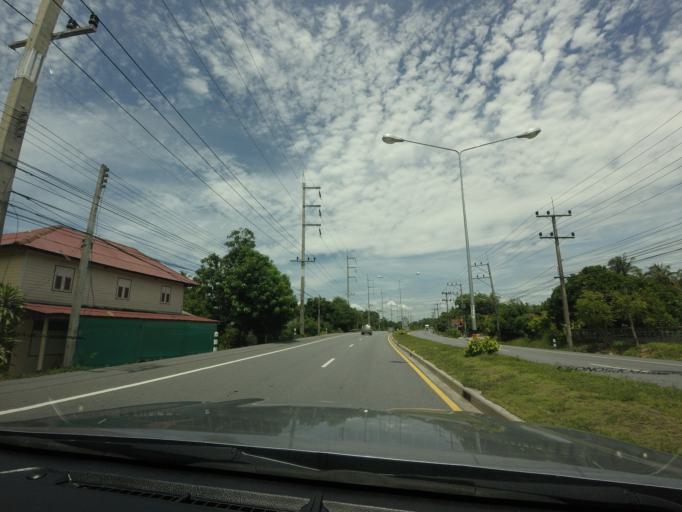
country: TH
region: Songkhla
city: Krasae Sin
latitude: 7.5696
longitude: 100.4104
